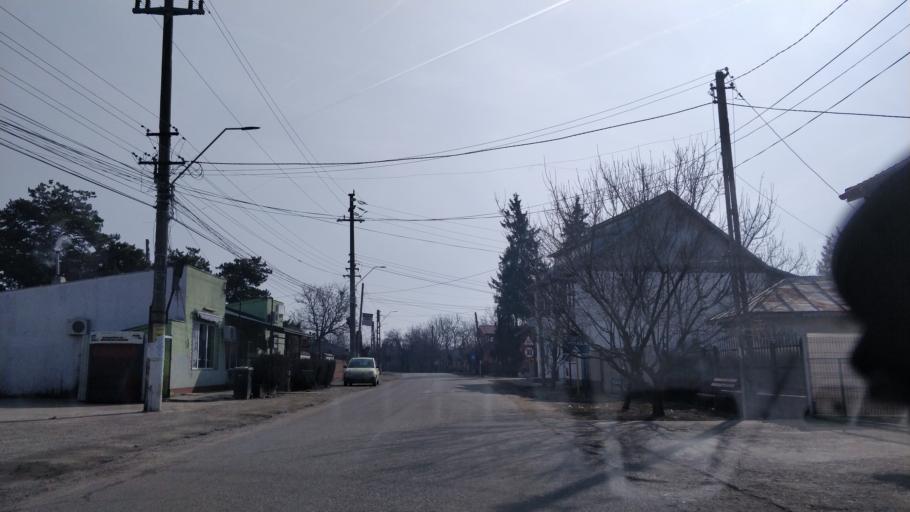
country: RO
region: Giurgiu
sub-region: Comuna Ulmi
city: Ulmi
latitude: 44.4706
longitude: 25.7670
